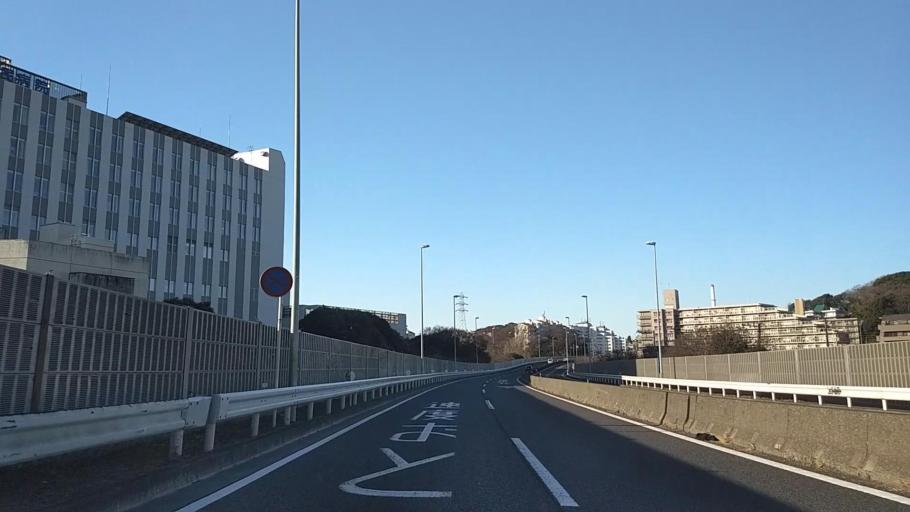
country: JP
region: Kanagawa
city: Fujisawa
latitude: 35.3522
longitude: 139.4829
